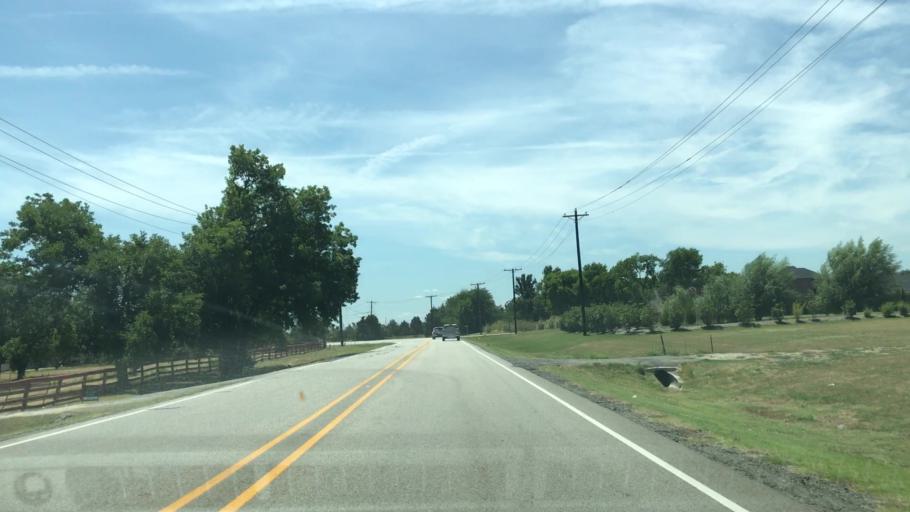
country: US
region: Texas
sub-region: Collin County
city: Saint Paul
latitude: 33.0377
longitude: -96.5504
